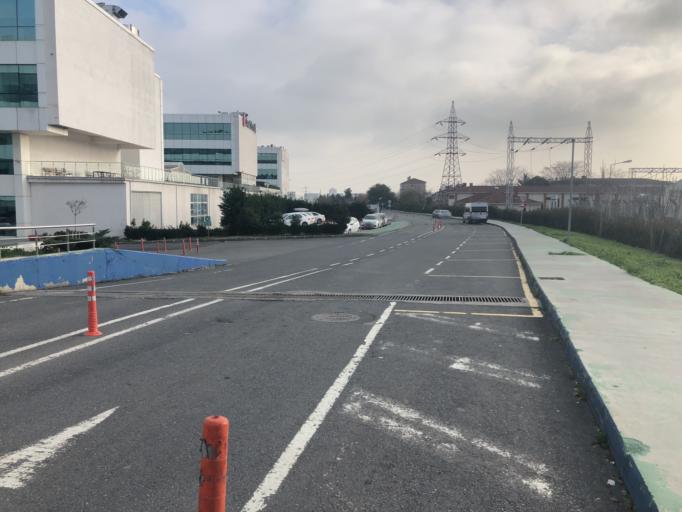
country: TR
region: Istanbul
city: merter keresteciler
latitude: 41.0186
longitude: 28.8885
